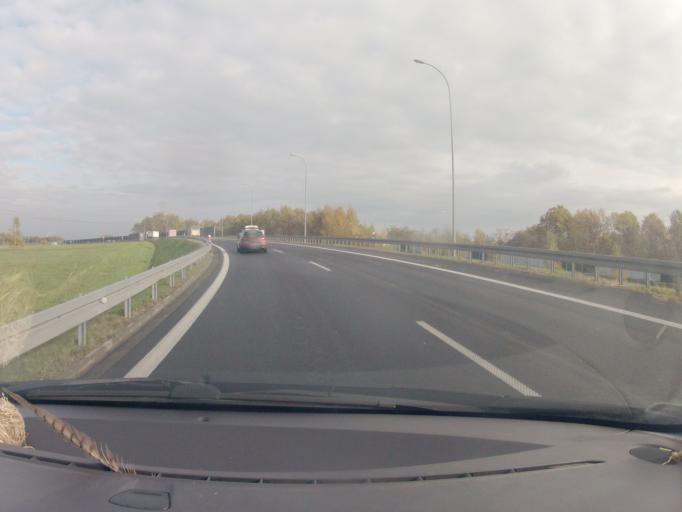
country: PL
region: Lesser Poland Voivodeship
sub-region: Powiat wielicki
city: Czarnochowice
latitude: 50.0104
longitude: 20.0645
